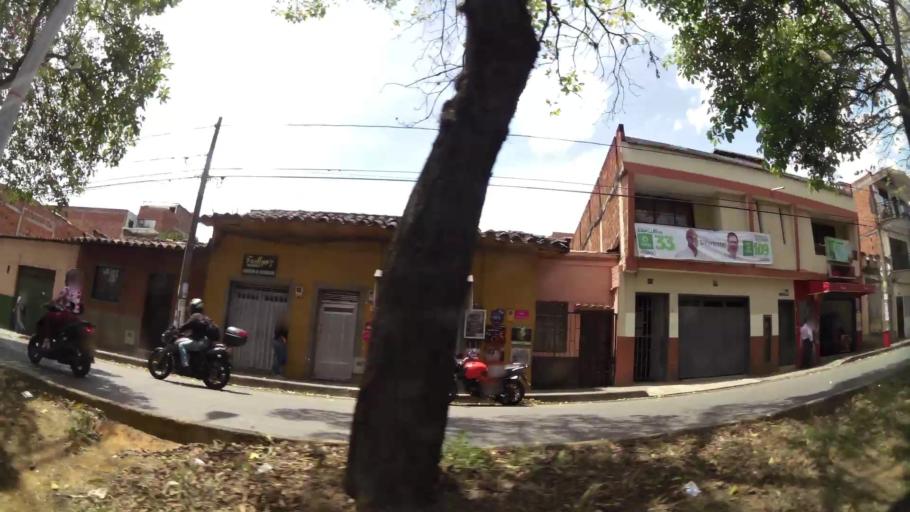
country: CO
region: Antioquia
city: Bello
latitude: 6.3395
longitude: -75.5626
